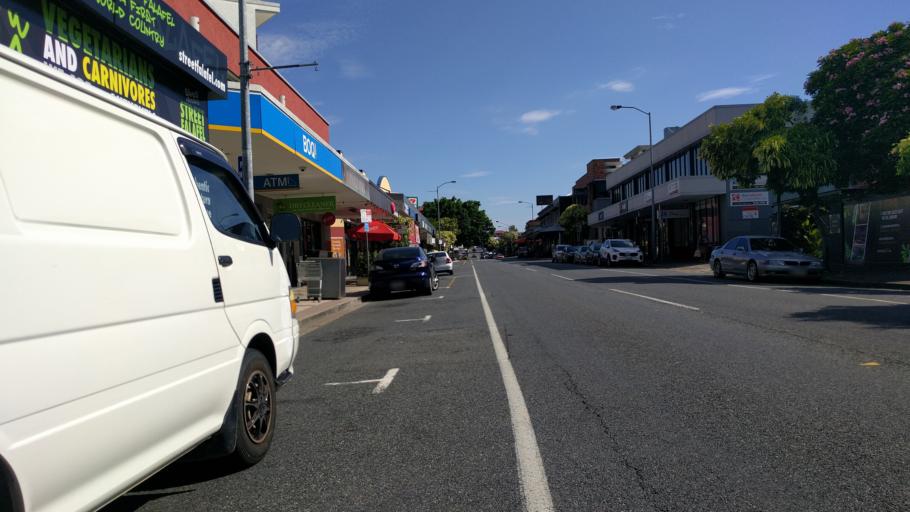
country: AU
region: Queensland
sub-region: Brisbane
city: South Brisbane
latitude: -27.4779
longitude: 153.0126
